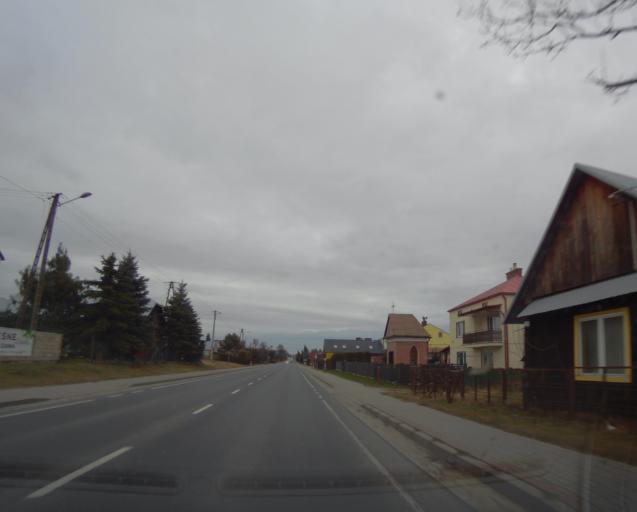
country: PL
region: Subcarpathian Voivodeship
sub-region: Powiat rzeszowski
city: Wolka Podlesna
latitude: 50.1343
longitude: 22.0685
